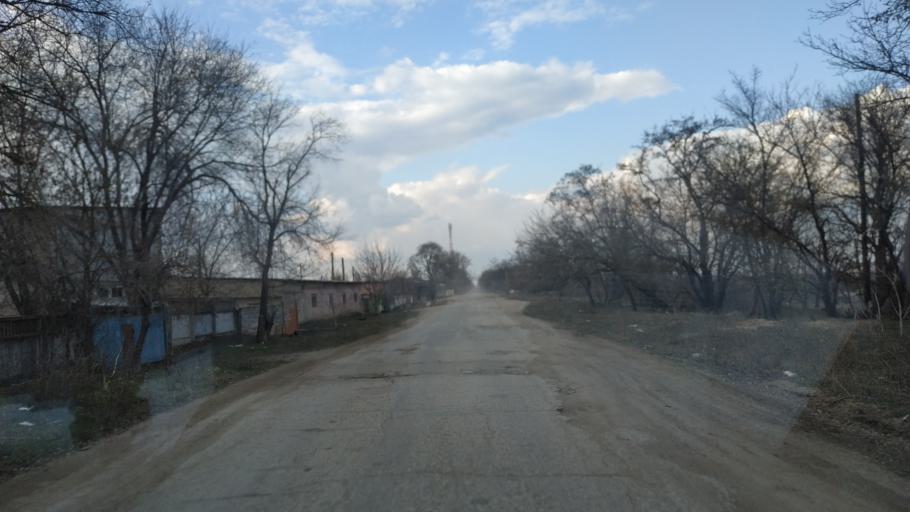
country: MD
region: Anenii Noi
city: Varnita
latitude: 46.8969
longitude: 29.4604
